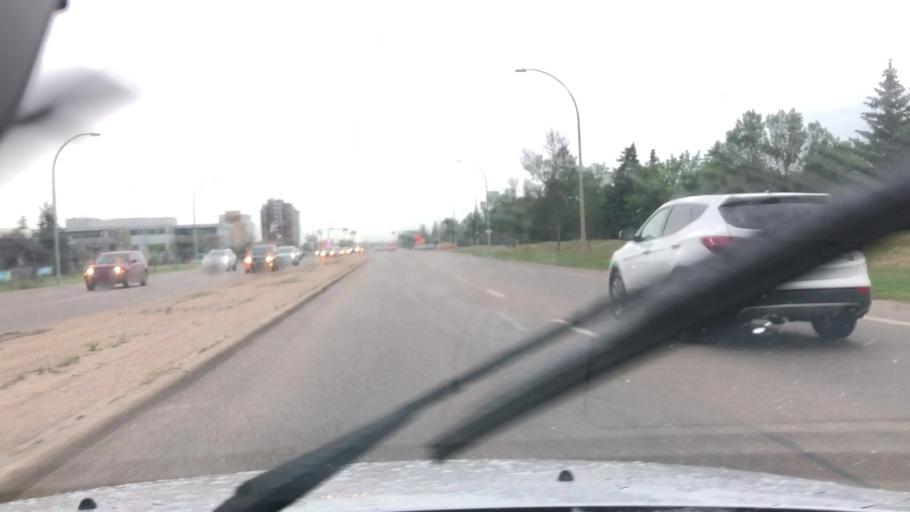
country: CA
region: Alberta
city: St. Albert
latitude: 53.5500
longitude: -113.6099
